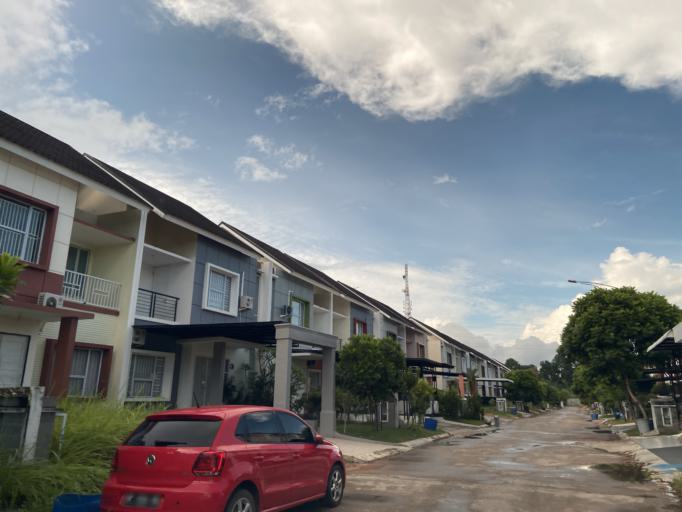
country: SG
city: Singapore
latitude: 1.0916
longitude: 104.0337
